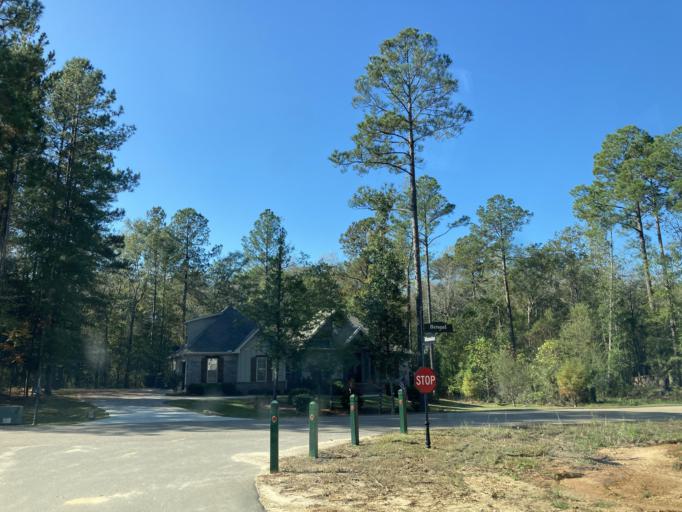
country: US
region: Mississippi
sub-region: Lamar County
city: Sumrall
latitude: 31.3290
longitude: -89.4876
